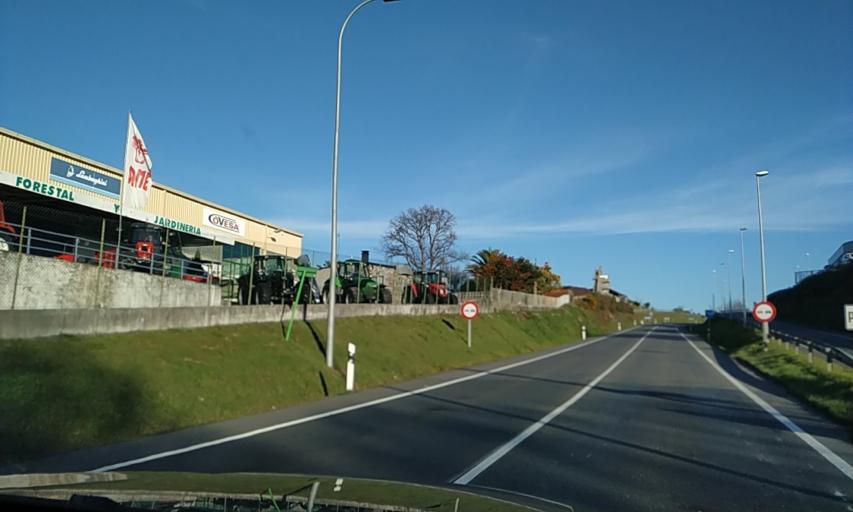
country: ES
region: Galicia
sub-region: Provincia de Pontevedra
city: Silleda
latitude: 42.6941
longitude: -8.2296
